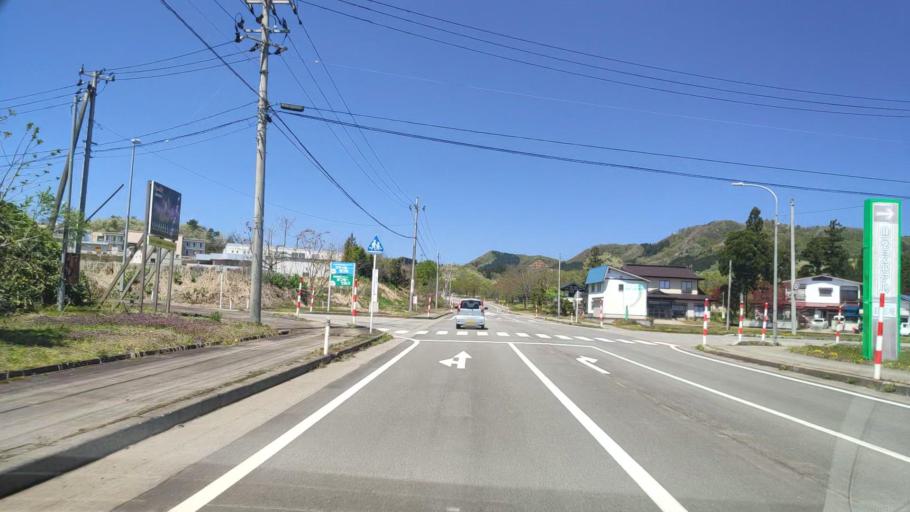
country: JP
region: Akita
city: Omagari
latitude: 39.4326
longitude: 140.4427
